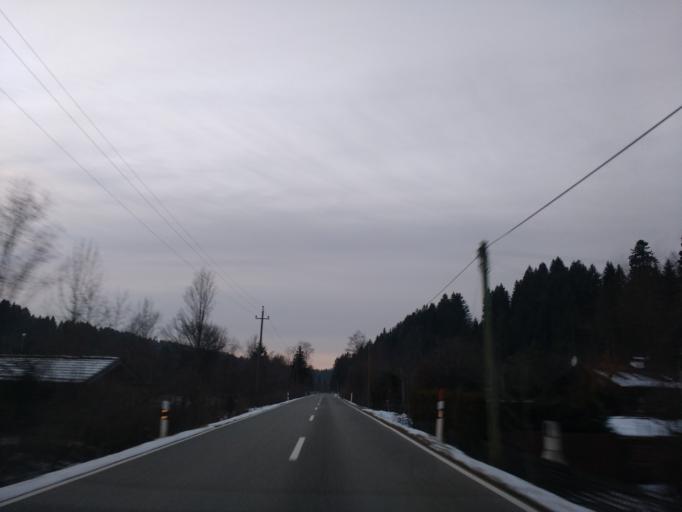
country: DE
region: Bavaria
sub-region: Swabia
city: Halblech
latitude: 47.6473
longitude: 10.8101
